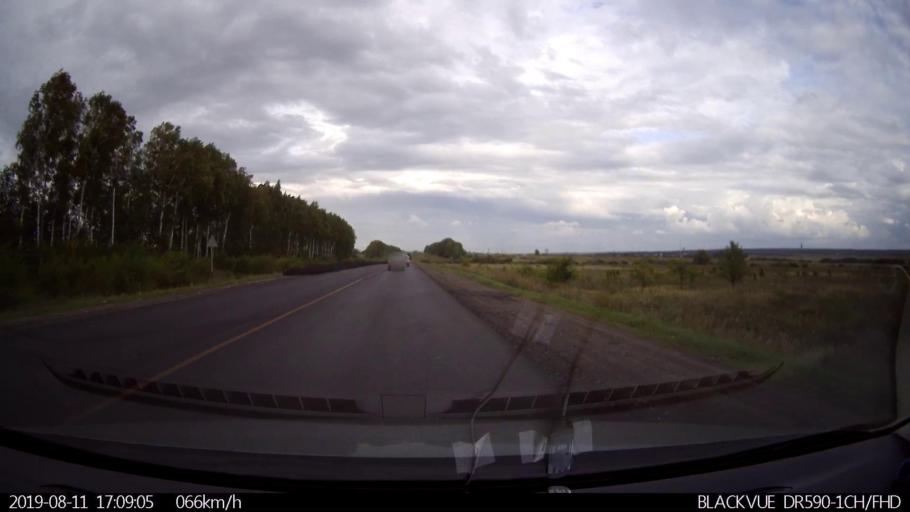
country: RU
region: Ulyanovsk
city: Mayna
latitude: 54.2943
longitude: 47.8506
